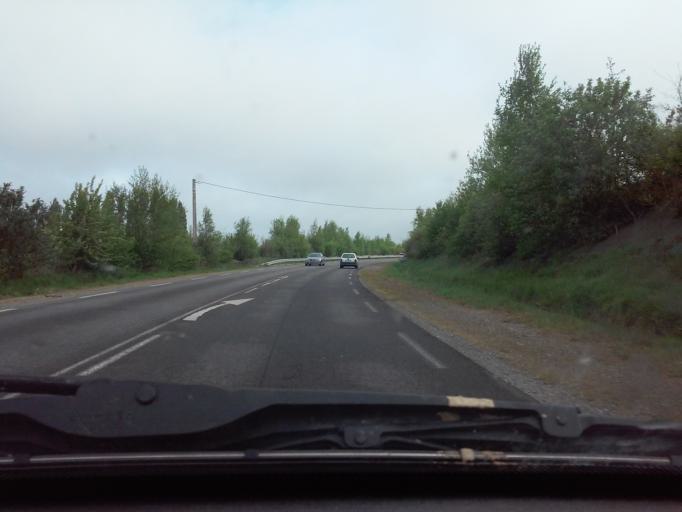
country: FR
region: Brittany
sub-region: Departement d'Ille-et-Vilaine
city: Pleurtuit
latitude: 48.5960
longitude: -2.0692
